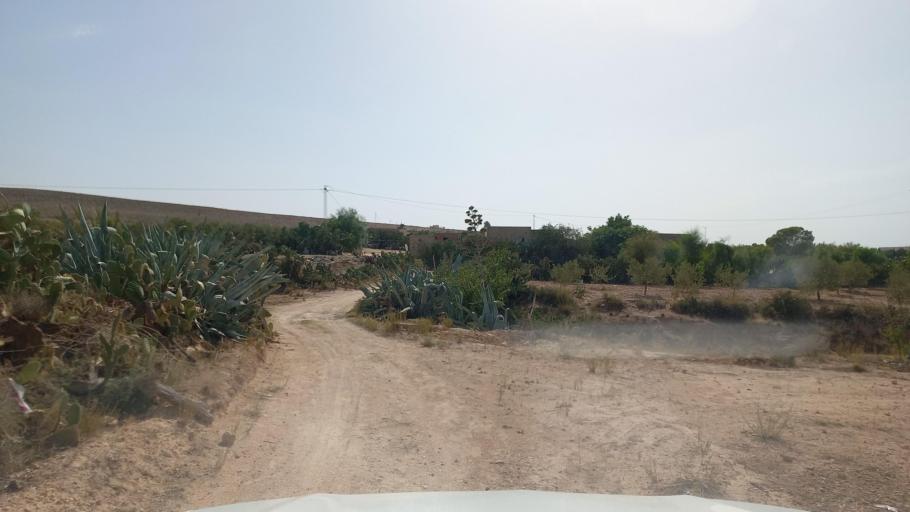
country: TN
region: Al Qasrayn
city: Kasserine
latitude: 35.2102
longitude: 8.9838
